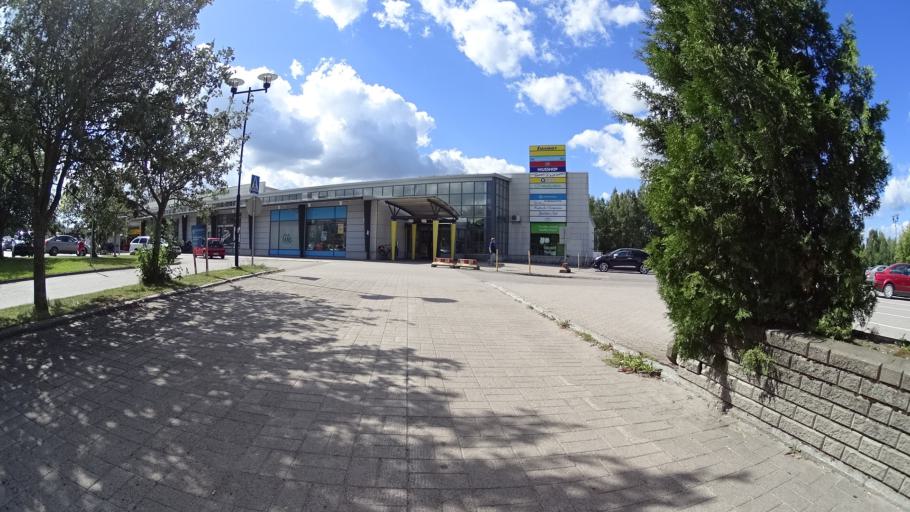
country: FI
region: Uusimaa
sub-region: Helsinki
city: Tuusula
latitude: 60.3975
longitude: 25.0197
